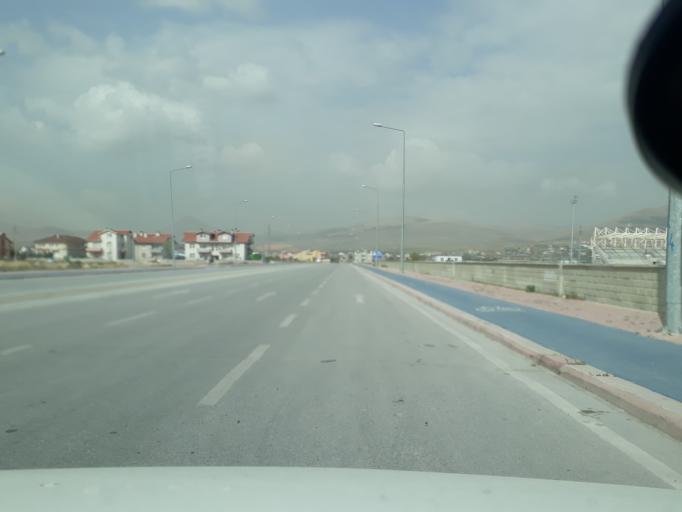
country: TR
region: Konya
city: Selcuklu
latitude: 37.9425
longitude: 32.4863
